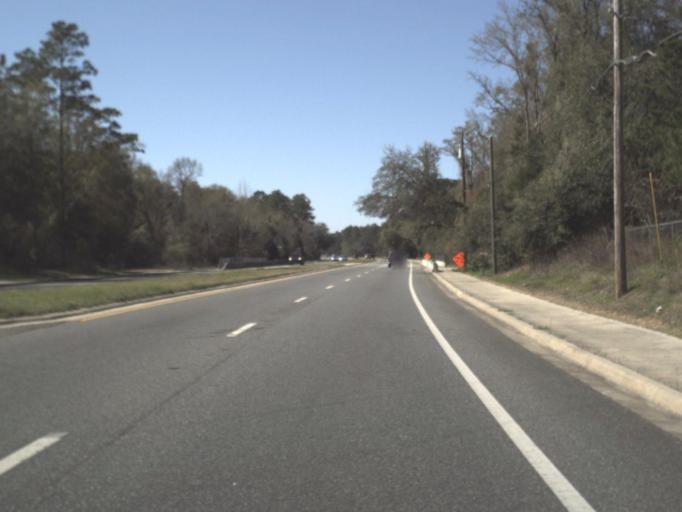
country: US
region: Florida
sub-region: Leon County
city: Woodville
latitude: 30.3587
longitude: -84.3019
